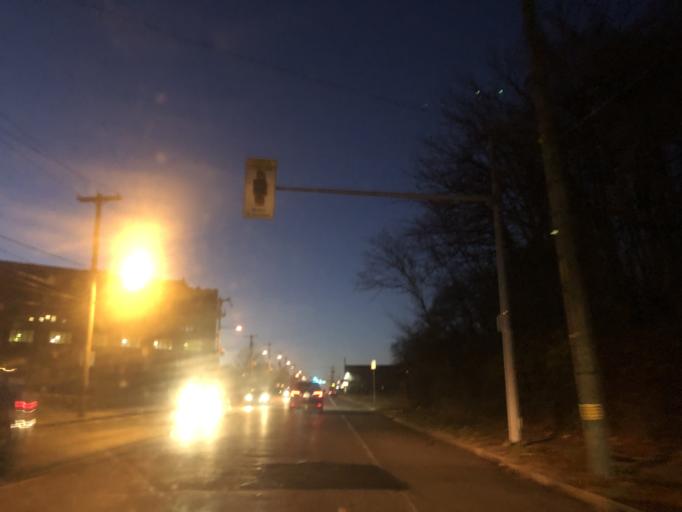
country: US
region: Pennsylvania
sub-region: Delaware County
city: Millbourne
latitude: 39.9810
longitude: -75.2361
